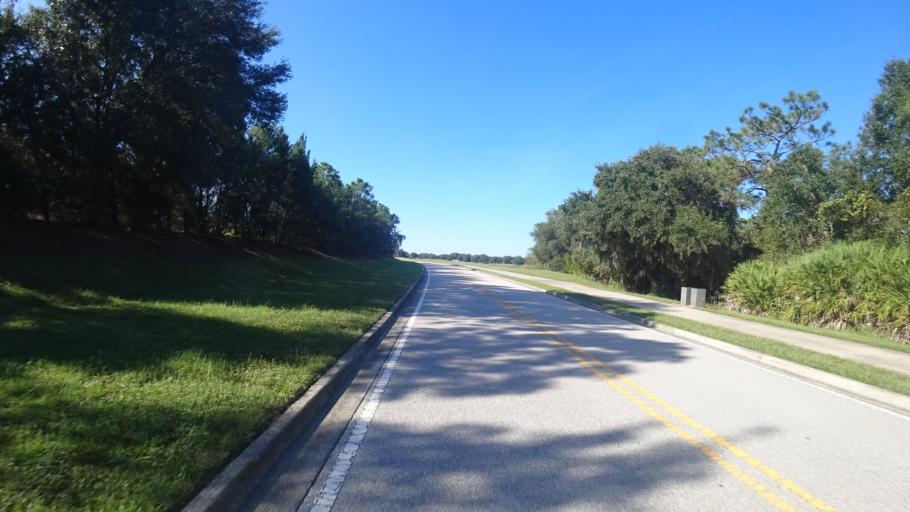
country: US
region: Florida
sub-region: Sarasota County
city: The Meadows
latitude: 27.4191
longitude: -82.4217
